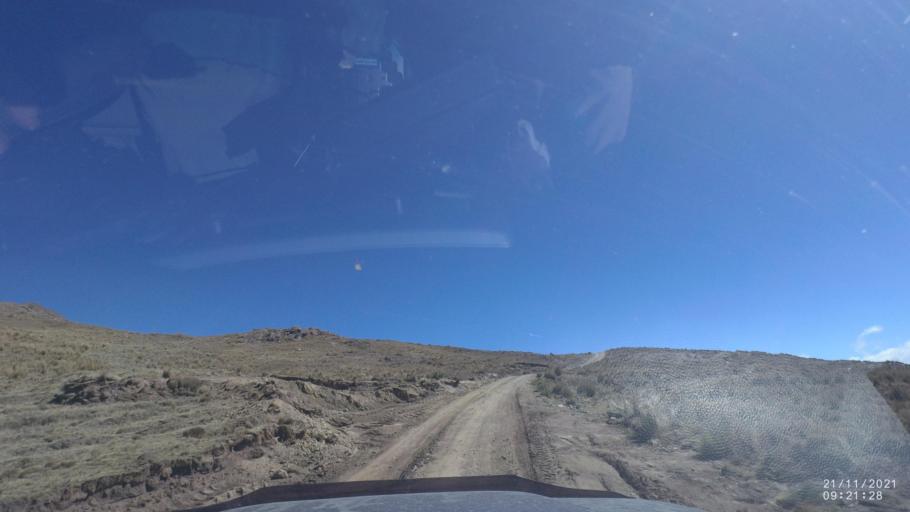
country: BO
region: Cochabamba
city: Cochabamba
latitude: -17.1058
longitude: -66.2489
